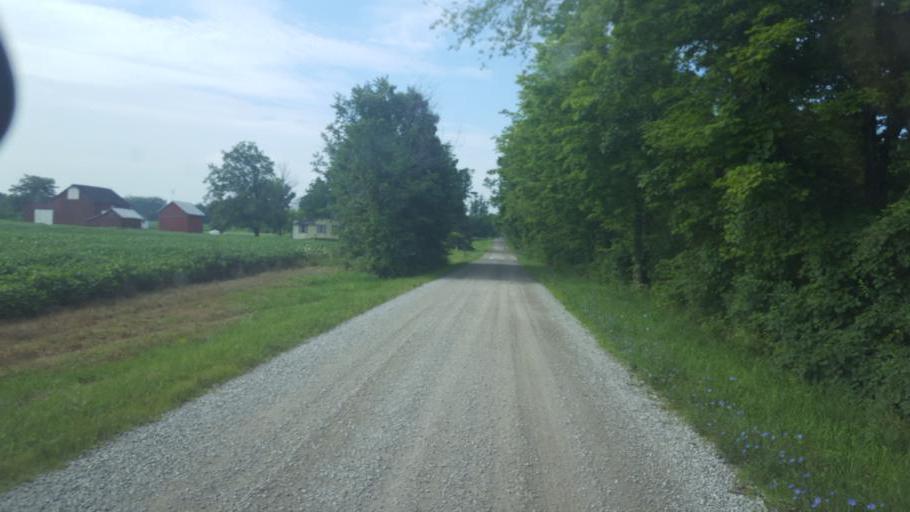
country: US
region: Ohio
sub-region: Delaware County
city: Ashley
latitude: 40.3726
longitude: -82.8837
